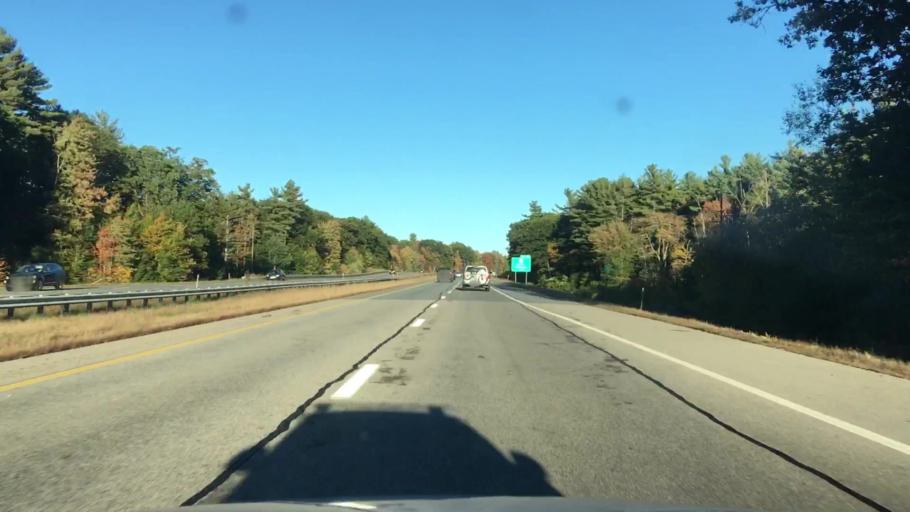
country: US
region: New Hampshire
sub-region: Rockingham County
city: Exeter
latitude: 43.0021
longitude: -70.9662
